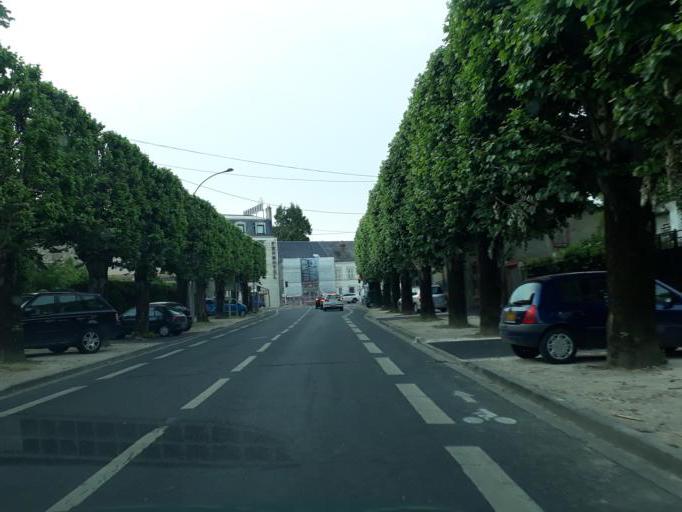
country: FR
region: Centre
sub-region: Departement du Loiret
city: Saint-Jean-le-Blanc
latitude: 47.9025
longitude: 1.9314
